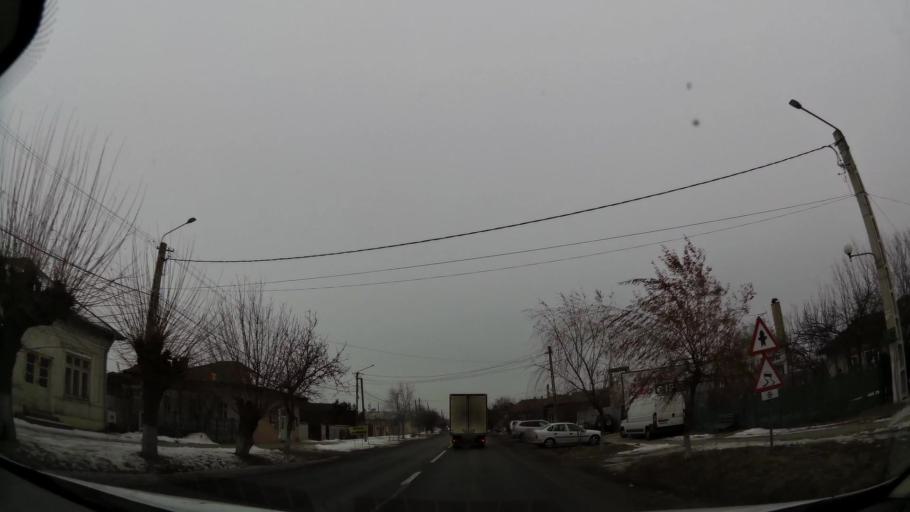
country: RO
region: Dambovita
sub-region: Comuna Racari
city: Racari
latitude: 44.6227
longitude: 25.7500
